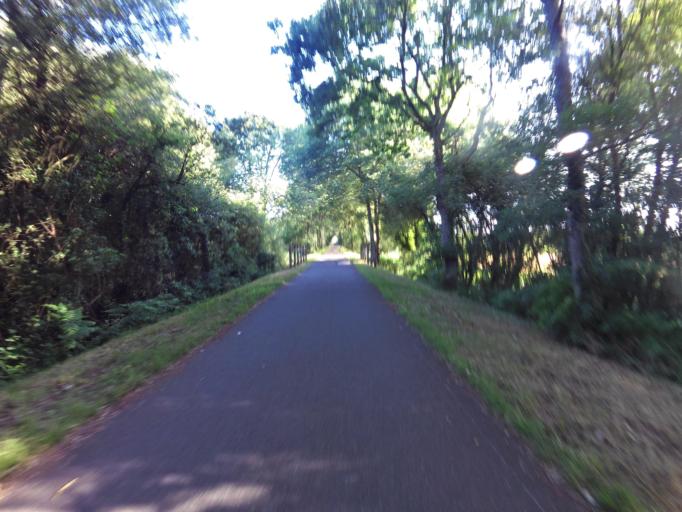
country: FR
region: Brittany
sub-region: Departement du Morbihan
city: Guillac
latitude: 47.8849
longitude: -2.4364
